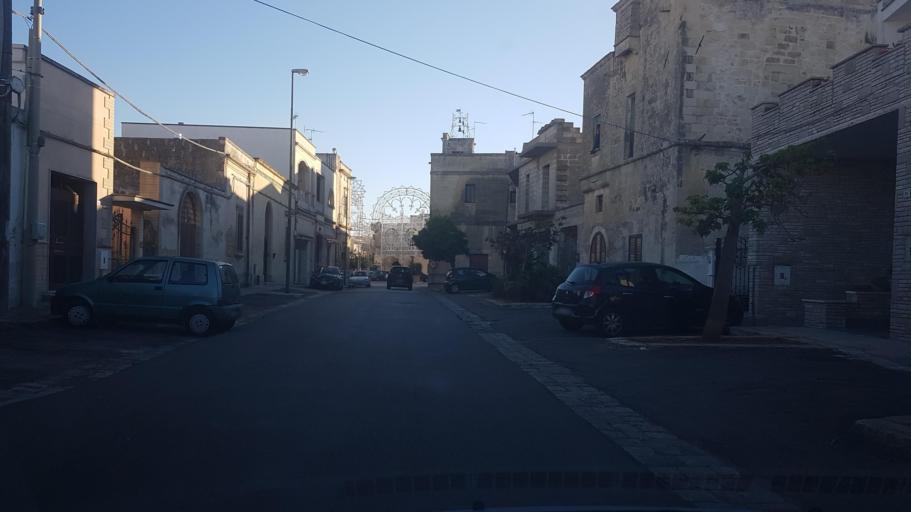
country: IT
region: Apulia
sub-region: Provincia di Lecce
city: Struda
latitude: 40.3211
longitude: 18.2829
